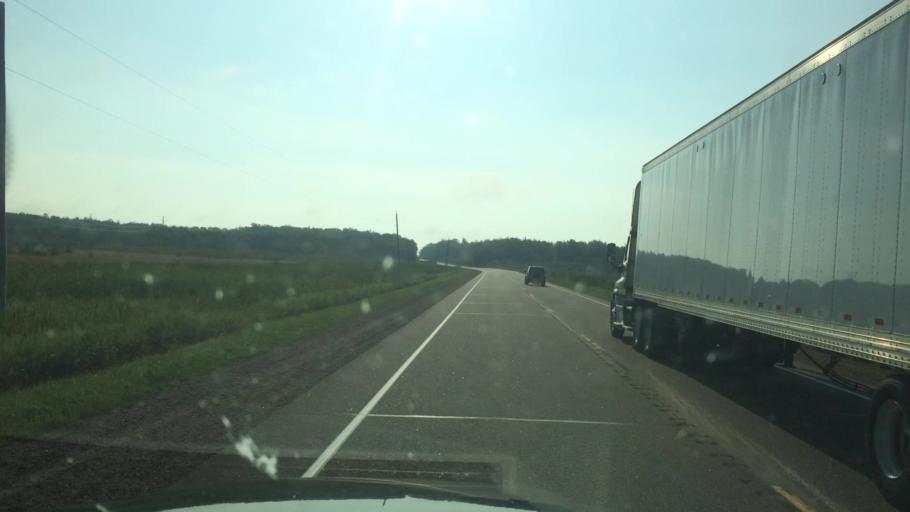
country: US
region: Wisconsin
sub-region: Langlade County
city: Antigo
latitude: 45.1471
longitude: -89.3991
